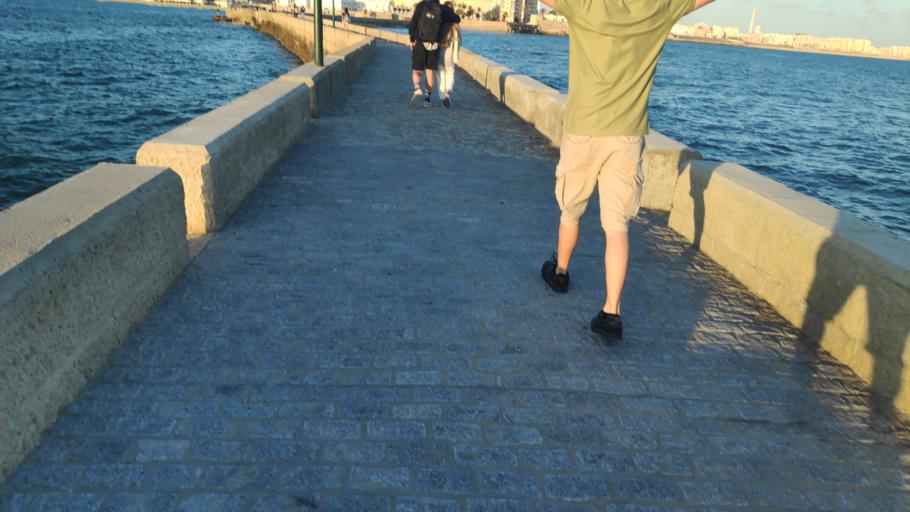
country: ES
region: Andalusia
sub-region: Provincia de Cadiz
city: Cadiz
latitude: 36.5279
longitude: -6.3111
